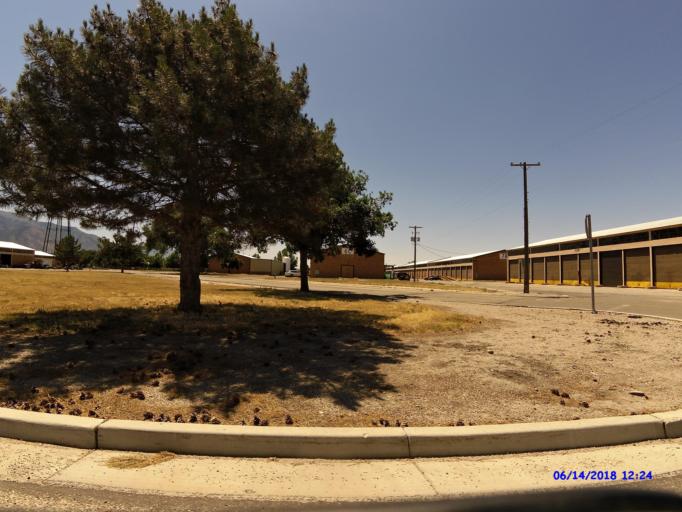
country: US
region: Utah
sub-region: Weber County
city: Harrisville
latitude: 41.2613
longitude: -111.9963
